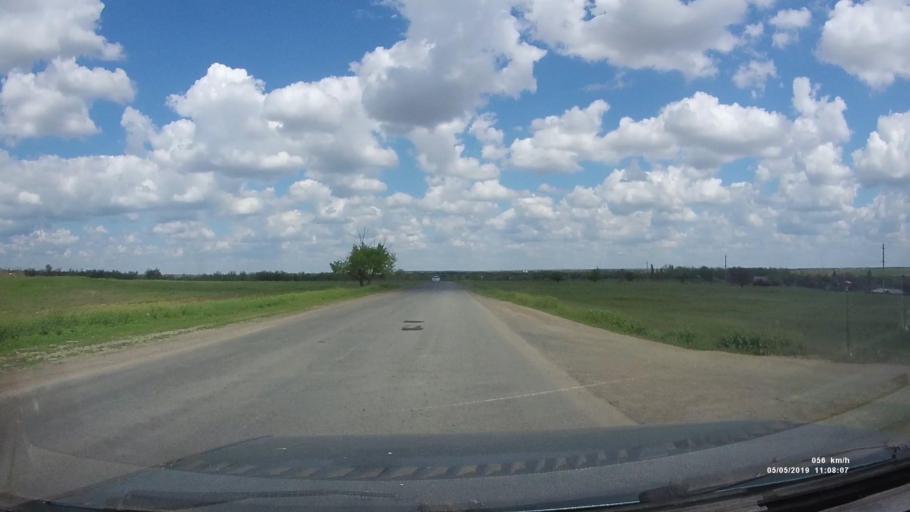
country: RU
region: Rostov
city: Ust'-Donetskiy
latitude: 47.7309
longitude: 40.9143
